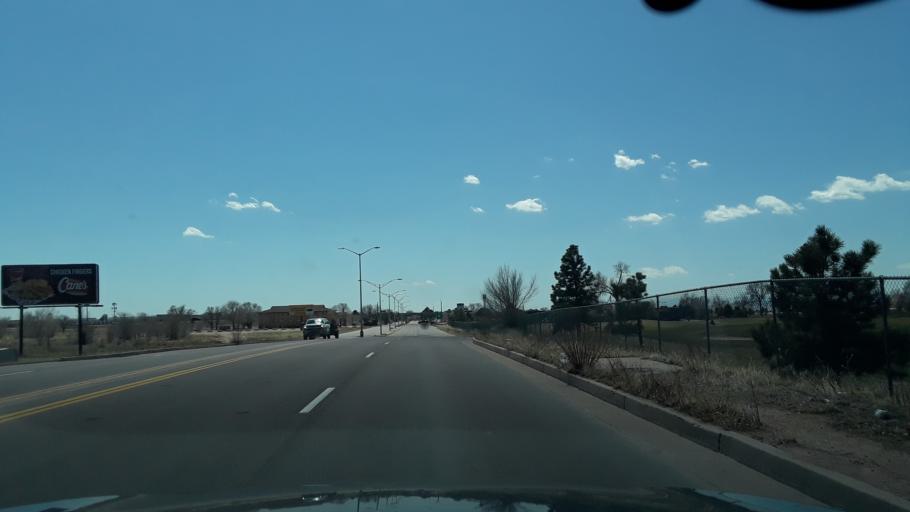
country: US
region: Colorado
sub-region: El Paso County
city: Cimarron Hills
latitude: 38.8437
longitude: -104.7015
